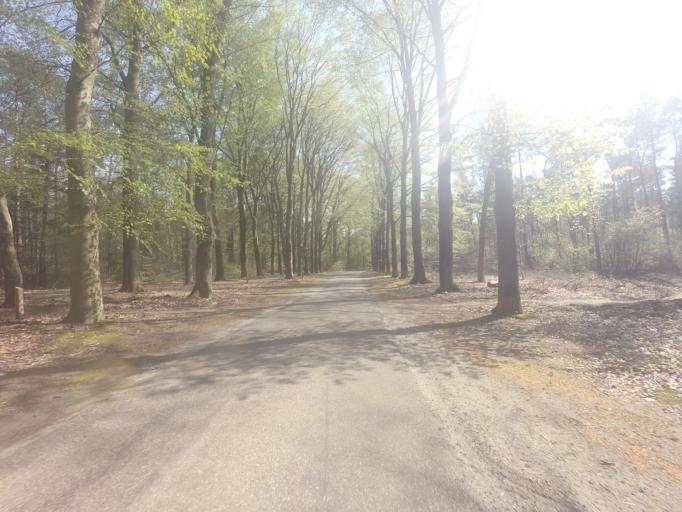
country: NL
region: North Holland
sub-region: Gemeente Hilversum
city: Hilversum
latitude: 52.1872
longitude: 5.2239
